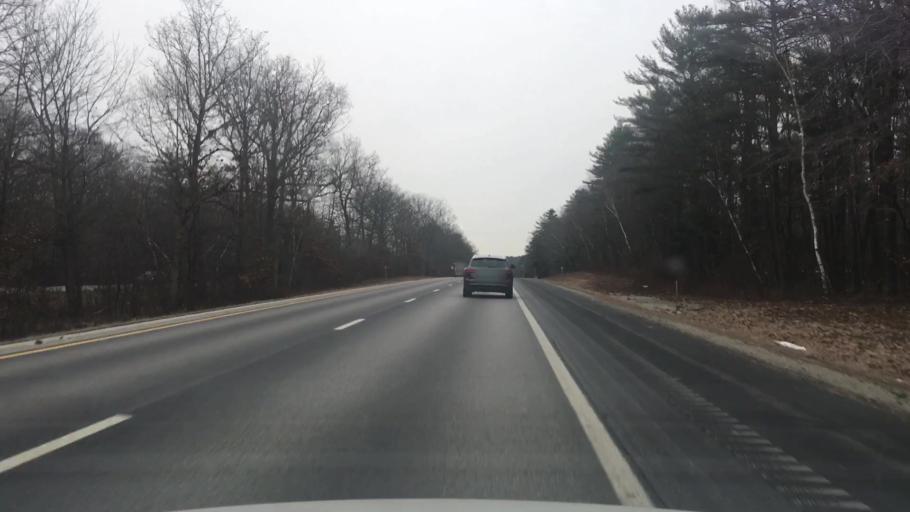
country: US
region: New Hampshire
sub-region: Merrimack County
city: Concord
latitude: 43.1739
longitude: -71.5544
